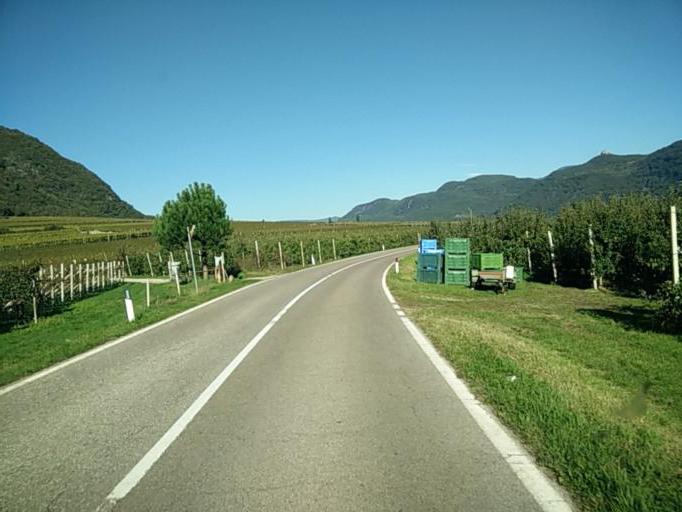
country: IT
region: Trentino-Alto Adige
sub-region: Bolzano
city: Termeno
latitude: 46.3562
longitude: 11.2498
